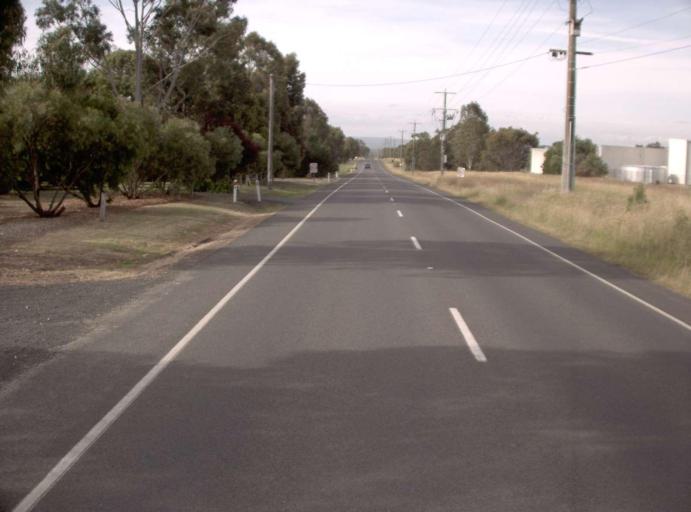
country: AU
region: Victoria
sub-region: Latrobe
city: Traralgon
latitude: -38.1873
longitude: 146.5612
